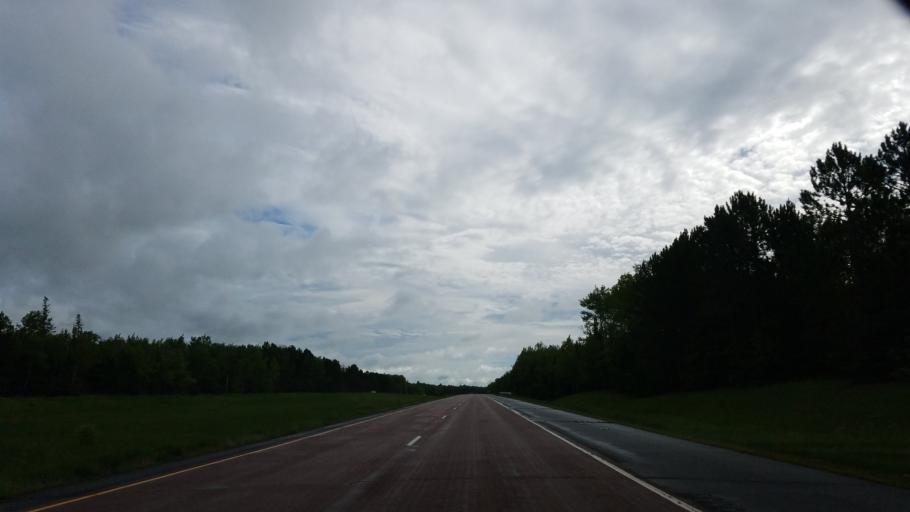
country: US
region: Minnesota
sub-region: Lake County
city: Two Harbors
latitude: 46.9198
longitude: -91.8669
